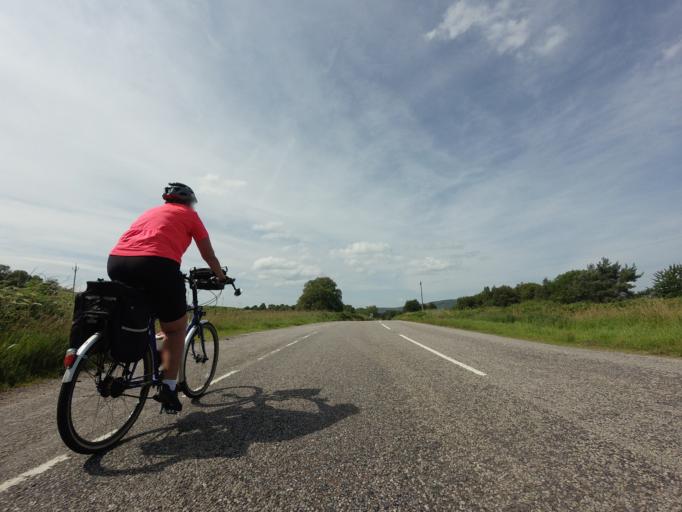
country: GB
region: Scotland
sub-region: Highland
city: Alness
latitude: 57.8568
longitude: -4.2294
